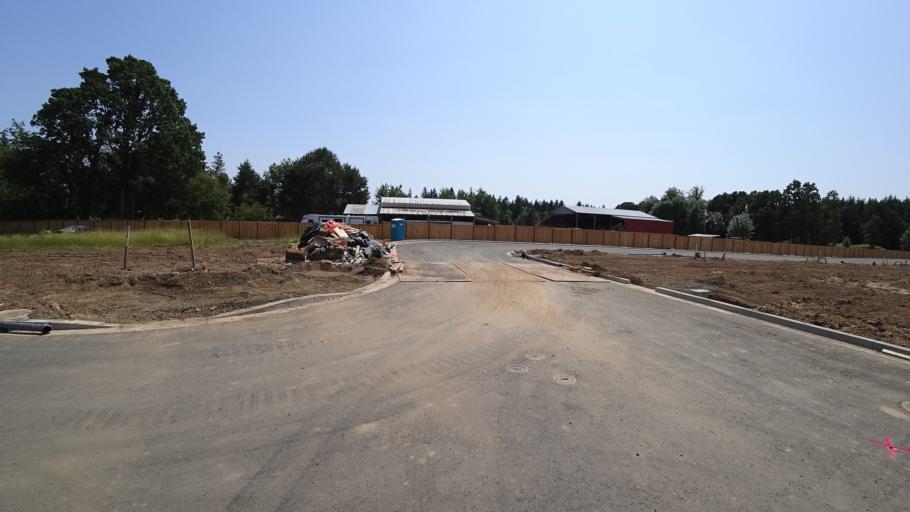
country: US
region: Oregon
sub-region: Washington County
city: Aloha
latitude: 45.4914
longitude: -122.9324
